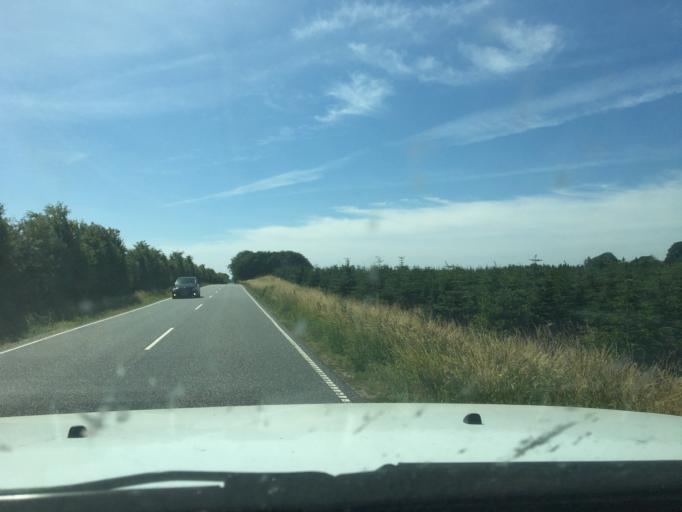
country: DK
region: Central Jutland
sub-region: Viborg Kommune
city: Bjerringbro
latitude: 56.5253
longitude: 9.6479
